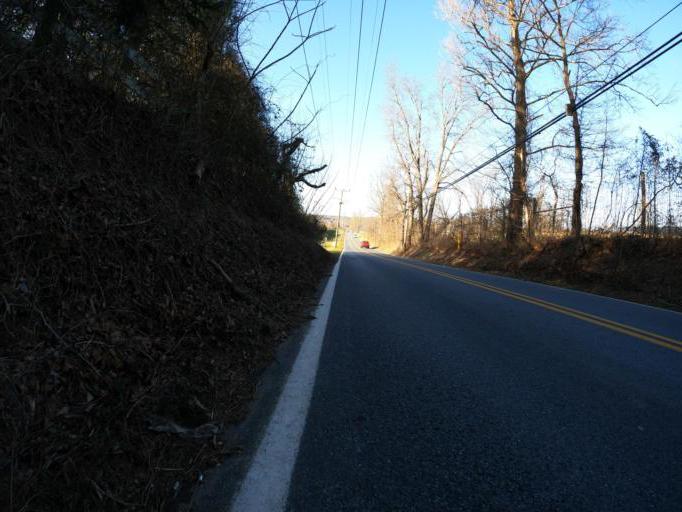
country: US
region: Maryland
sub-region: Howard County
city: Highland
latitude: 39.2328
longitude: -76.9389
